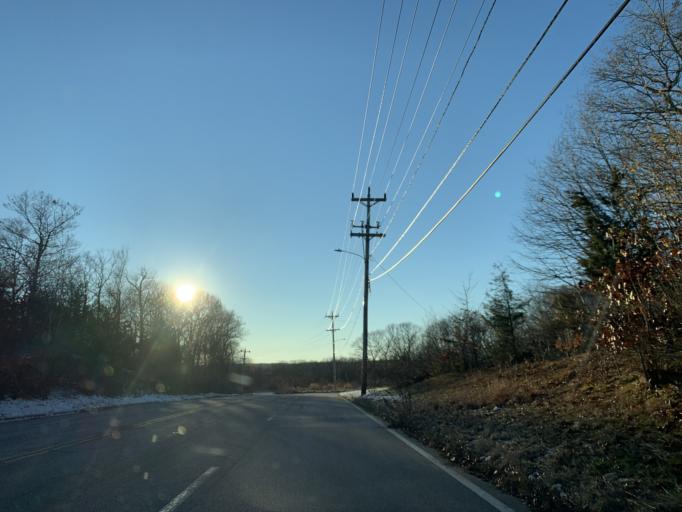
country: US
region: Rhode Island
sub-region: Kent County
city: West Warwick
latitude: 41.6637
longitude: -71.5221
